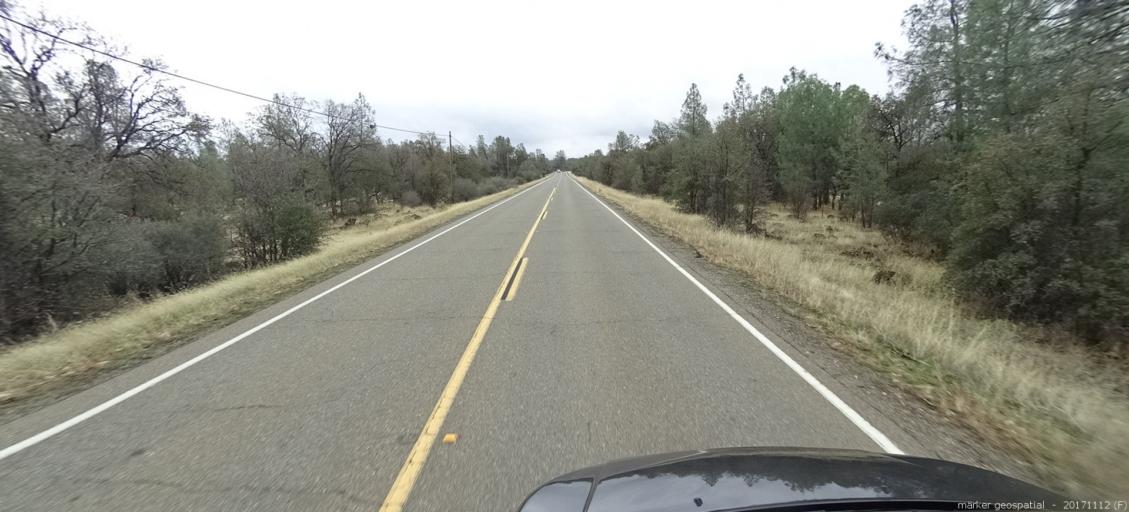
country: US
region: California
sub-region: Shasta County
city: Palo Cedro
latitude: 40.4837
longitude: -122.1115
